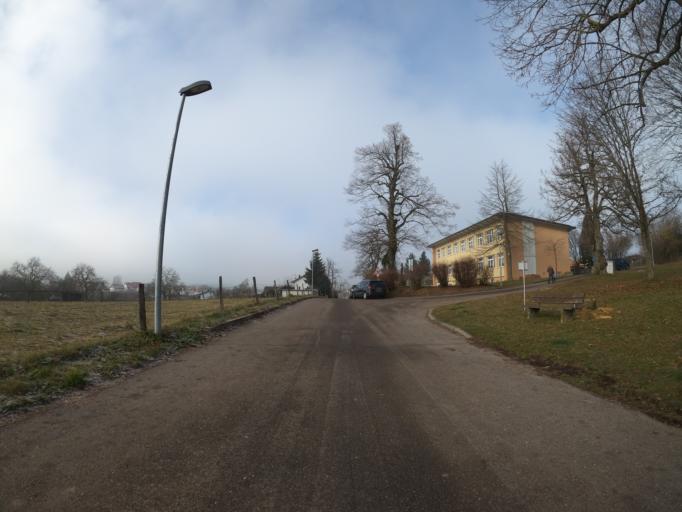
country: DE
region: Baden-Wuerttemberg
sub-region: Regierungsbezirk Stuttgart
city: Bad Uberkingen
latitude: 48.5847
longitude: 9.7681
